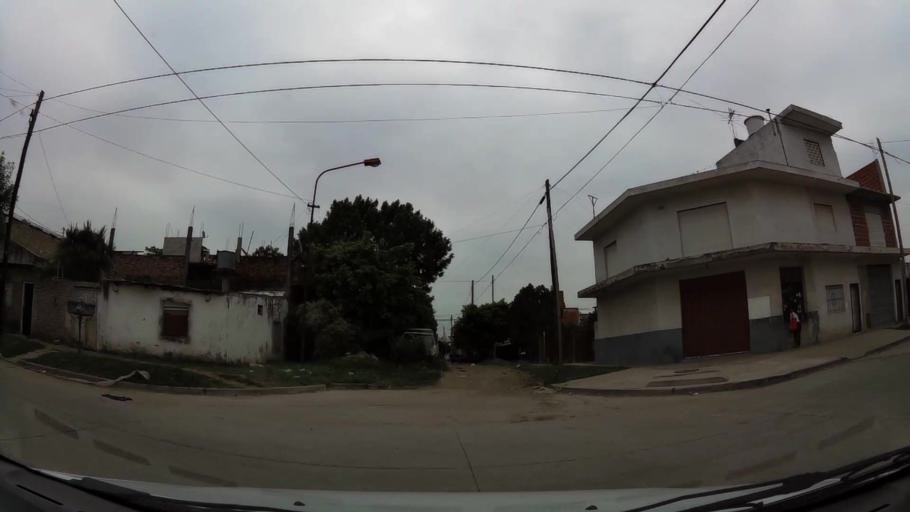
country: AR
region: Buenos Aires
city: San Justo
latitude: -34.7065
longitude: -58.5518
